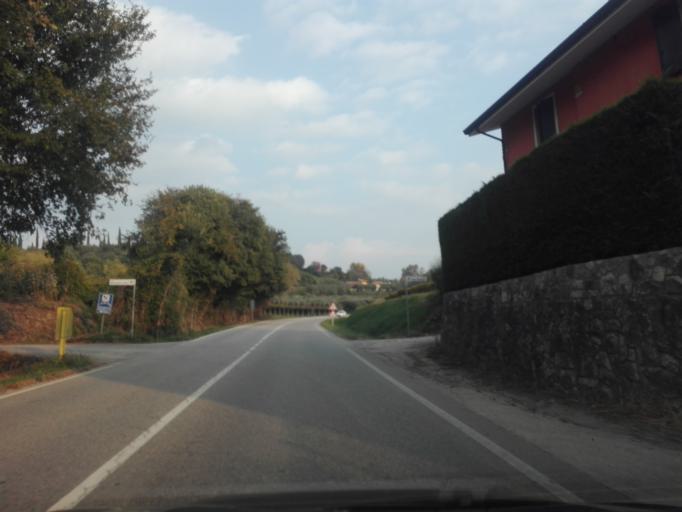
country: IT
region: Veneto
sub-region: Provincia di Verona
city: Lazise
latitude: 45.4974
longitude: 10.7524
